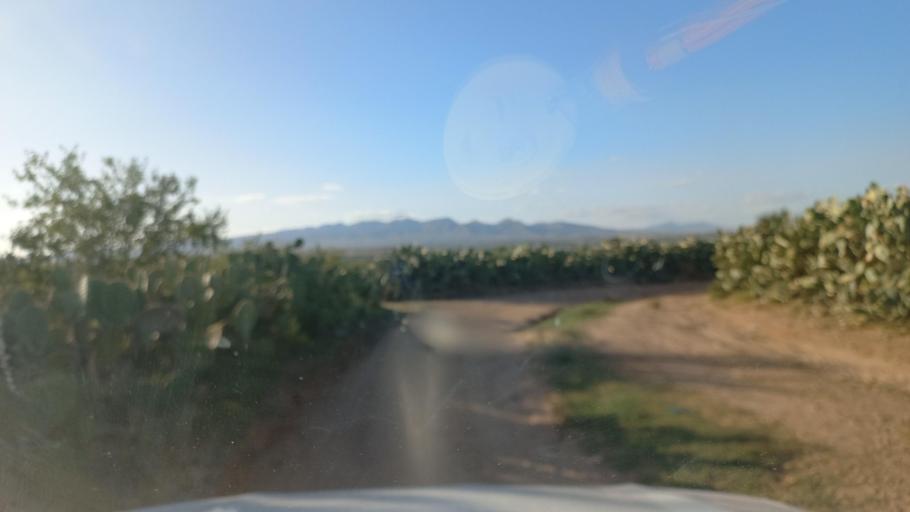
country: TN
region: Al Qasrayn
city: Sbiba
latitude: 35.3863
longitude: 9.1549
